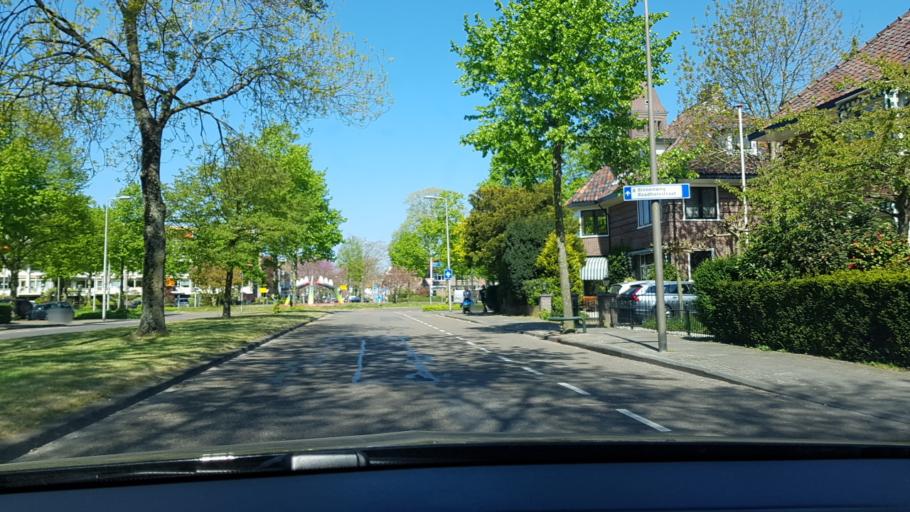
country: NL
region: North Holland
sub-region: Gemeente Heemstede
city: Heemstede
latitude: 52.3425
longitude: 4.6208
